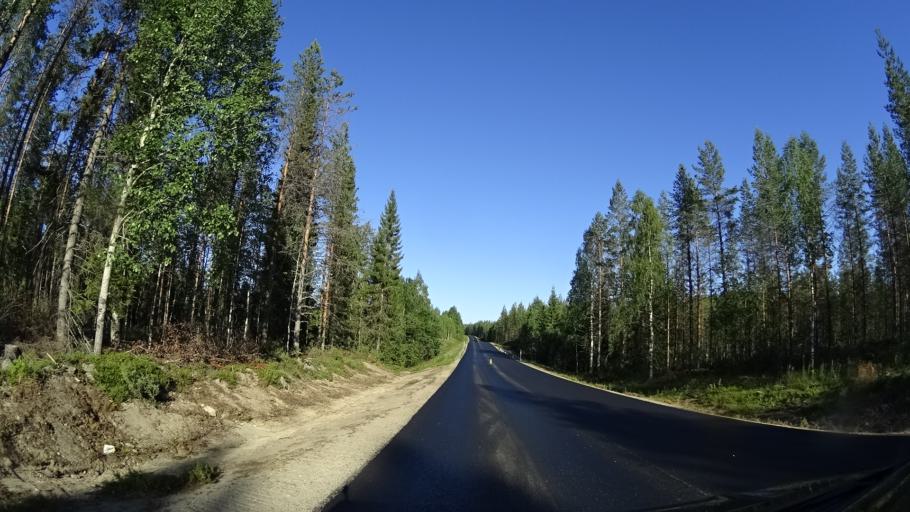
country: FI
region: North Karelia
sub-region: Pielisen Karjala
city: Valtimo
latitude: 63.5619
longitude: 28.5893
